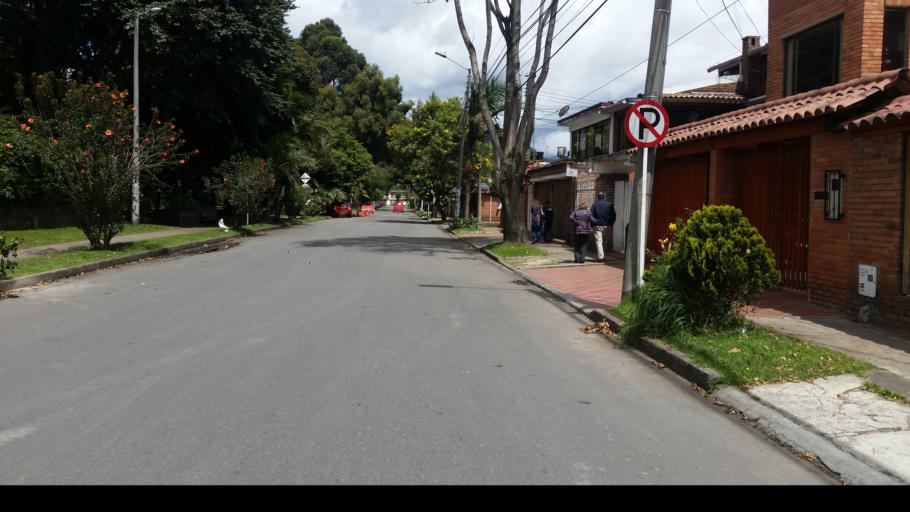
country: CO
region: Bogota D.C.
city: Bogota
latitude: 4.6470
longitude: -74.0913
